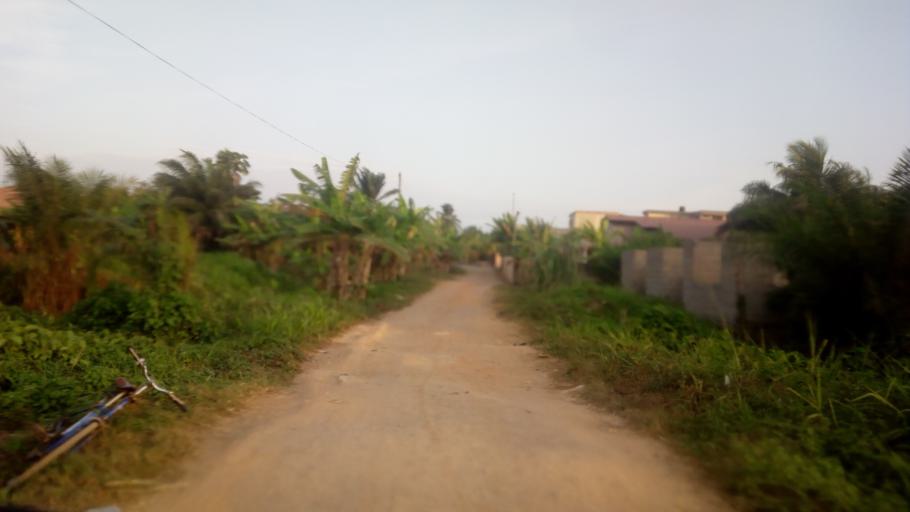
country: GH
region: Central
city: Cape Coast
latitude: 5.1270
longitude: -1.2787
